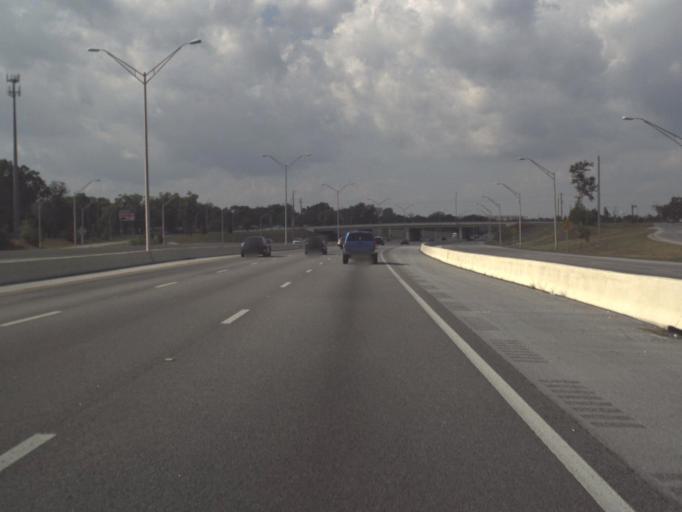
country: US
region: Florida
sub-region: Escambia County
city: Brent
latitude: 30.4778
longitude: -87.2297
